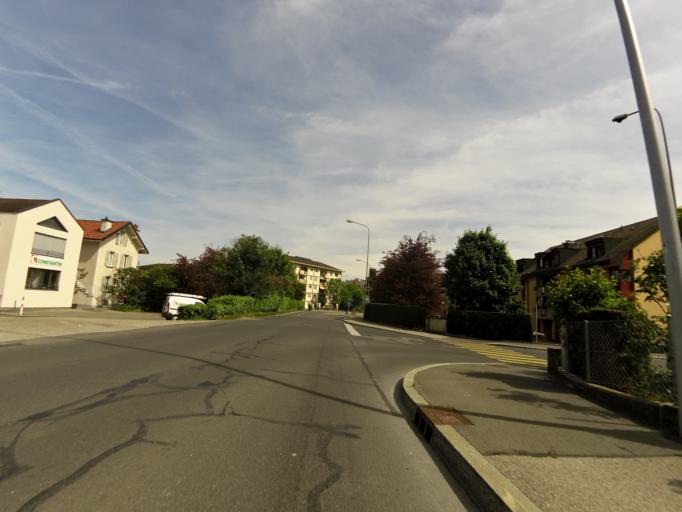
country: CH
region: Vaud
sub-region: Nyon District
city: Nyon
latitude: 46.3941
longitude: 6.2297
